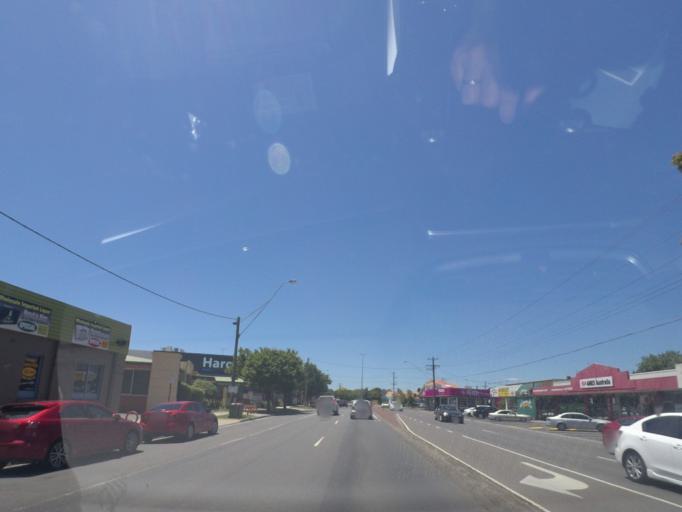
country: AU
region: Victoria
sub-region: Whittlesea
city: Epping
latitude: -37.6495
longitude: 145.0252
